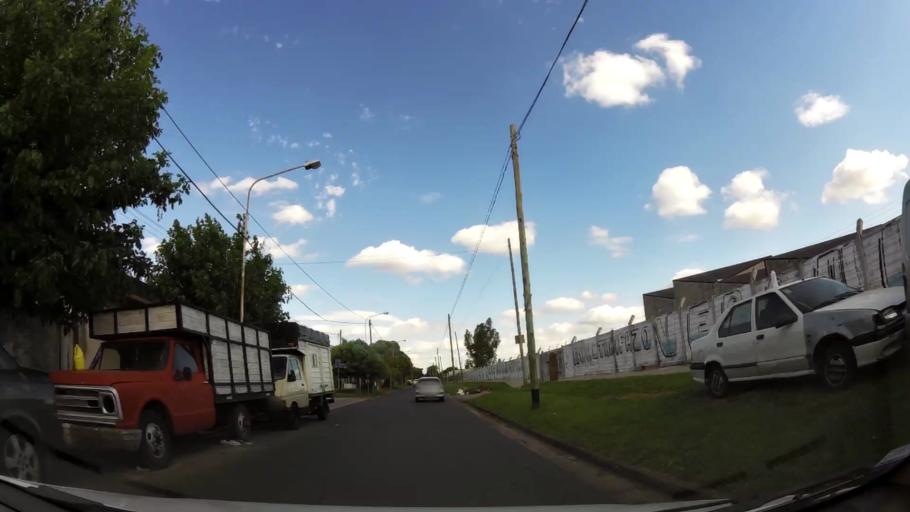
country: AR
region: Buenos Aires
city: San Justo
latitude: -34.6724
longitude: -58.5782
